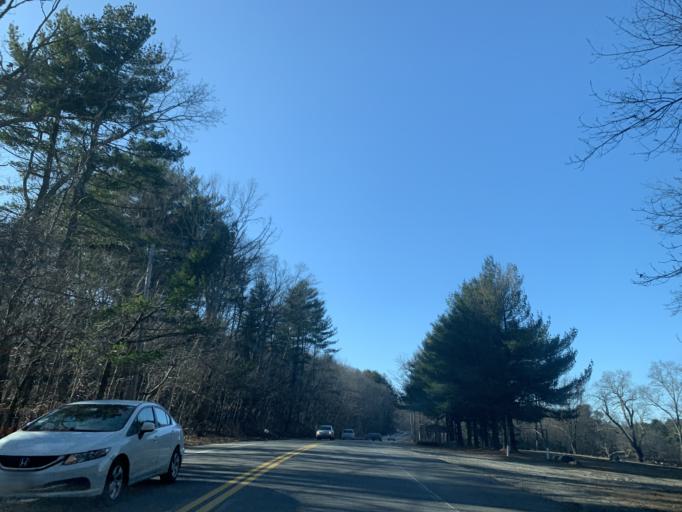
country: US
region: Massachusetts
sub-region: Middlesex County
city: Sudbury
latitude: 42.3556
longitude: -71.4679
